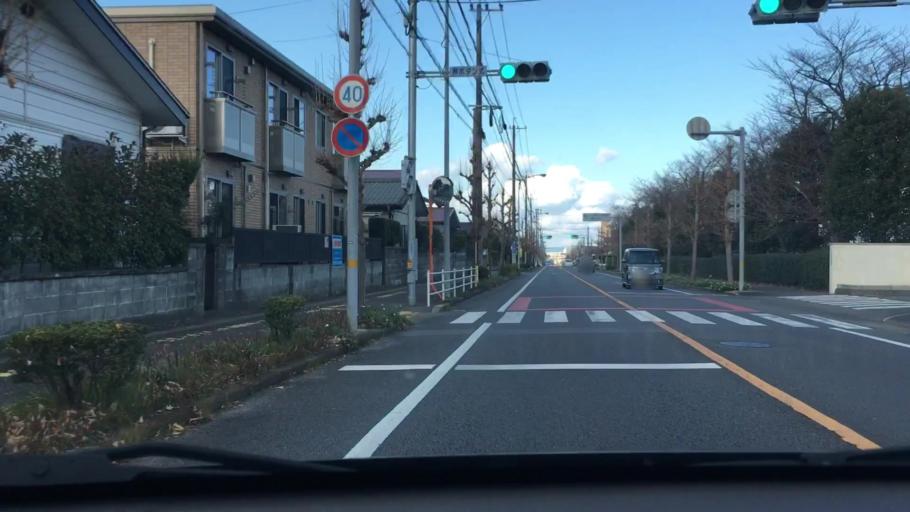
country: JP
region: Oita
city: Tsurusaki
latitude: 33.2155
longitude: 131.6588
